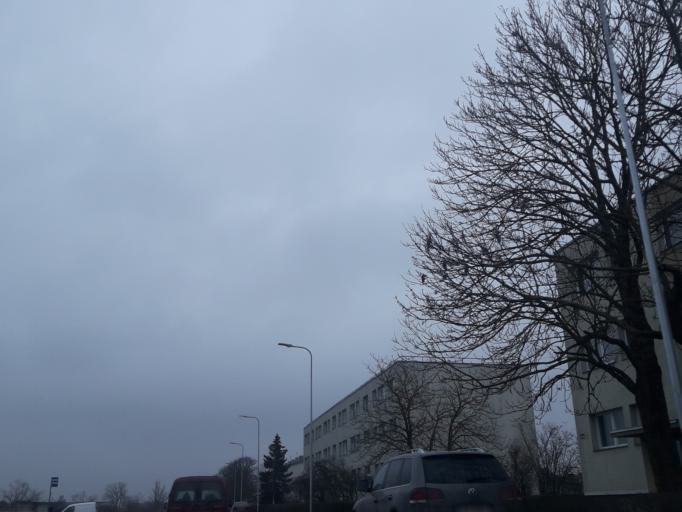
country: EE
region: Saare
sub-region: Kuressaare linn
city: Kuressaare
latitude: 58.2584
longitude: 22.4792
